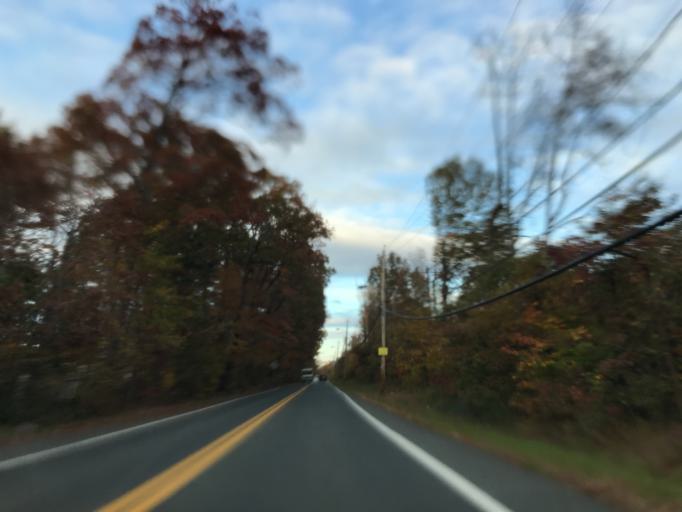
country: US
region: Maryland
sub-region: Baltimore County
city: Bowleys Quarters
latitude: 39.3655
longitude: -76.3662
